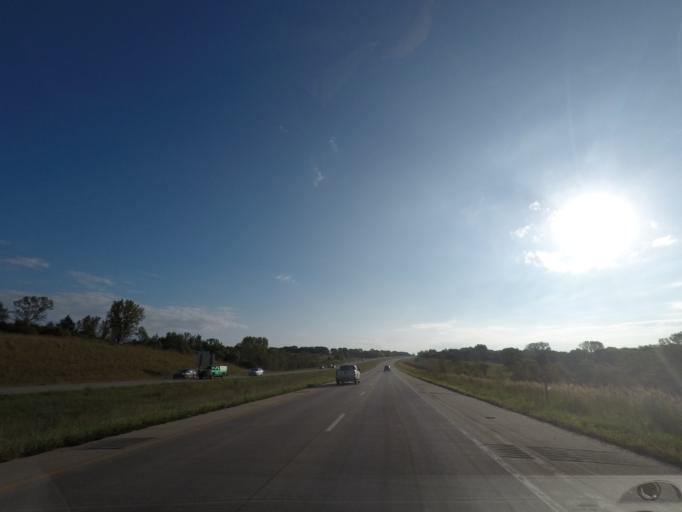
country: US
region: Iowa
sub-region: Warren County
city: Carlisle
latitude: 41.5101
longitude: -93.5560
